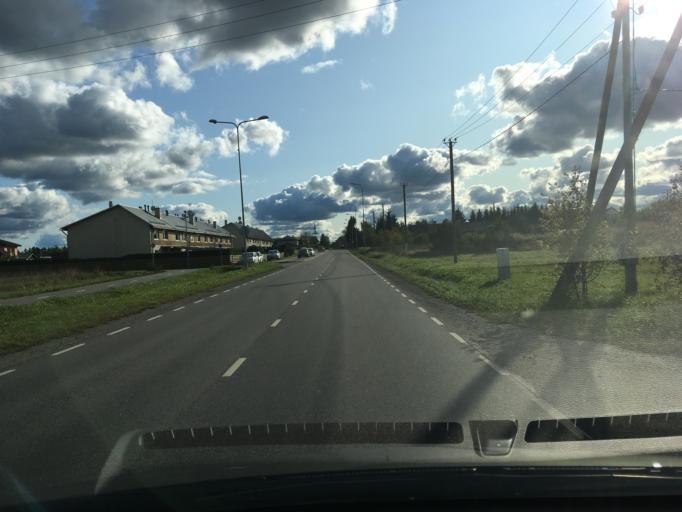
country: EE
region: Harju
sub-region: Joelaehtme vald
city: Loo
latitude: 59.4062
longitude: 24.9449
